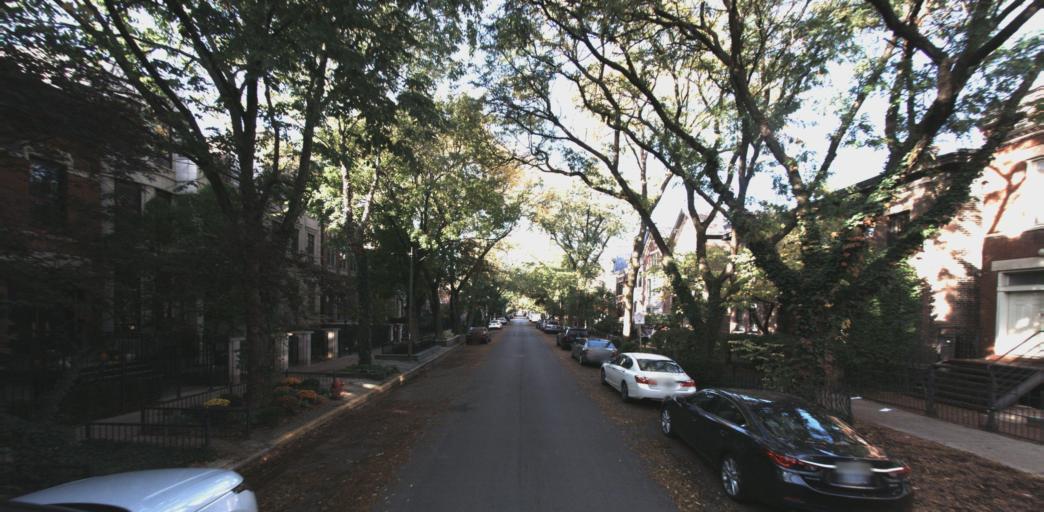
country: US
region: Illinois
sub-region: Cook County
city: Chicago
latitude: 41.9206
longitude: -87.6559
